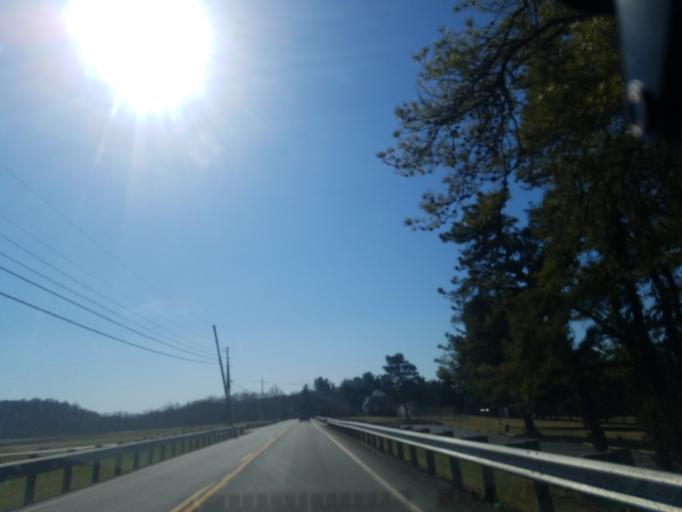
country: US
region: Ohio
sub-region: Tuscarawas County
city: Rockford
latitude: 40.5259
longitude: -81.2860
